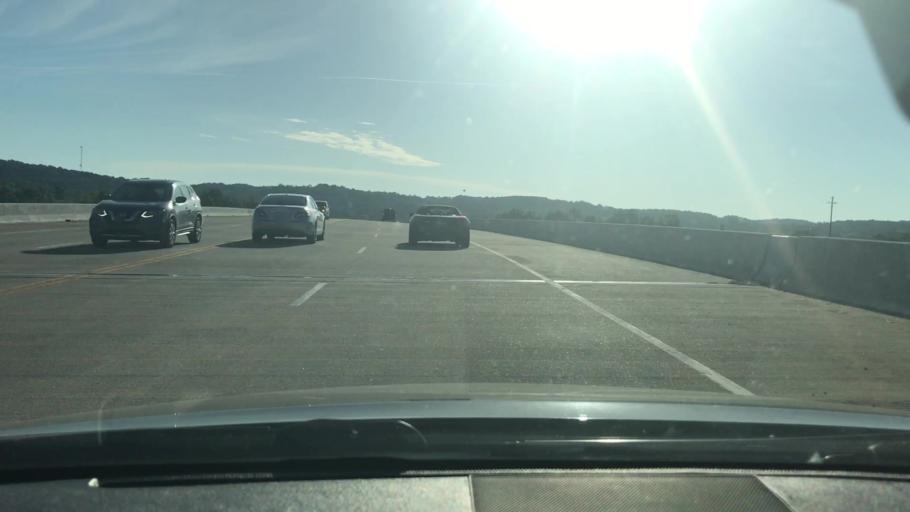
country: US
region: Tennessee
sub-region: Cheatham County
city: Ashland City
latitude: 36.2699
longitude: -87.0780
